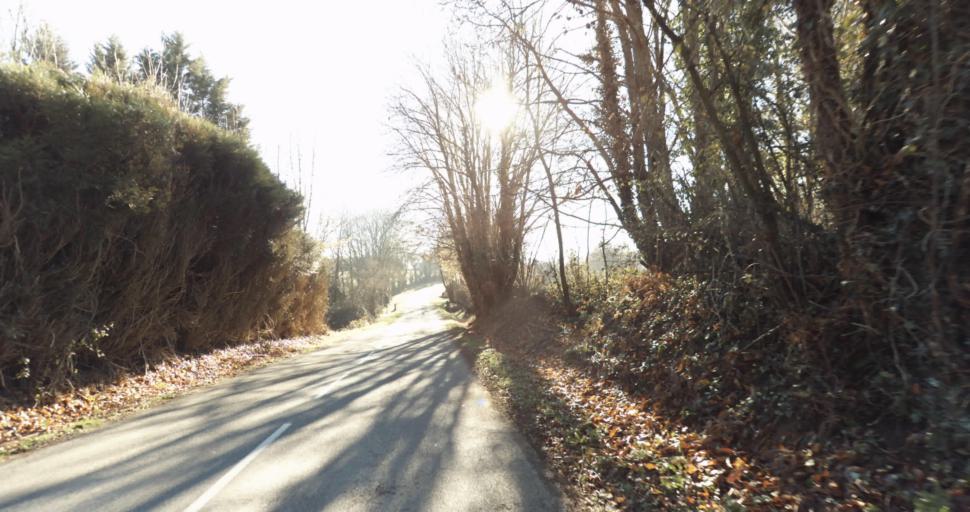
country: FR
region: Aquitaine
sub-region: Departement des Pyrenees-Atlantiques
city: Morlaas
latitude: 43.3344
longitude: -0.2441
